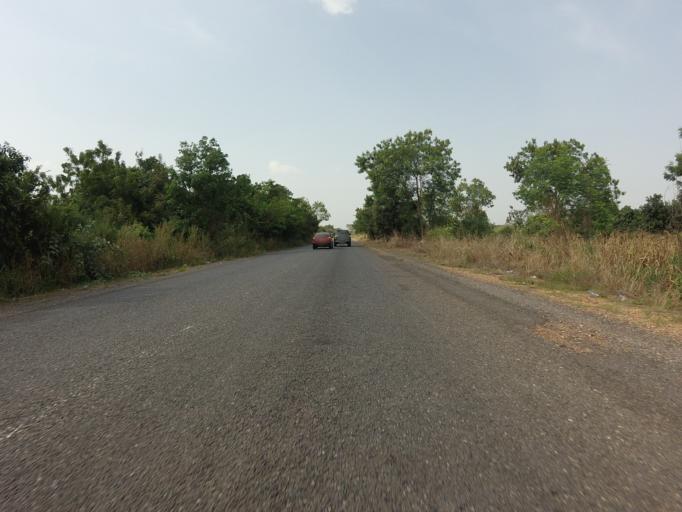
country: GH
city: Akropong
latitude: 6.0112
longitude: 0.0082
